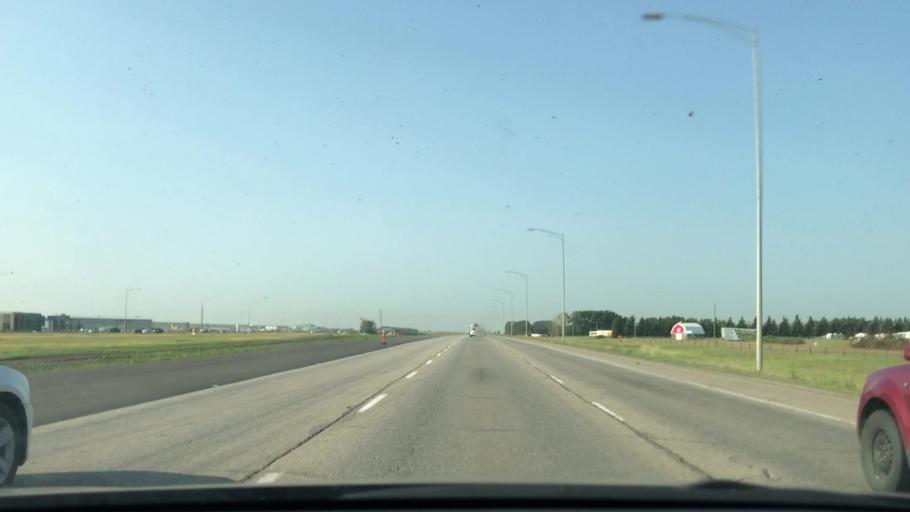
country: CA
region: Alberta
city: Leduc
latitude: 53.3707
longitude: -113.5284
